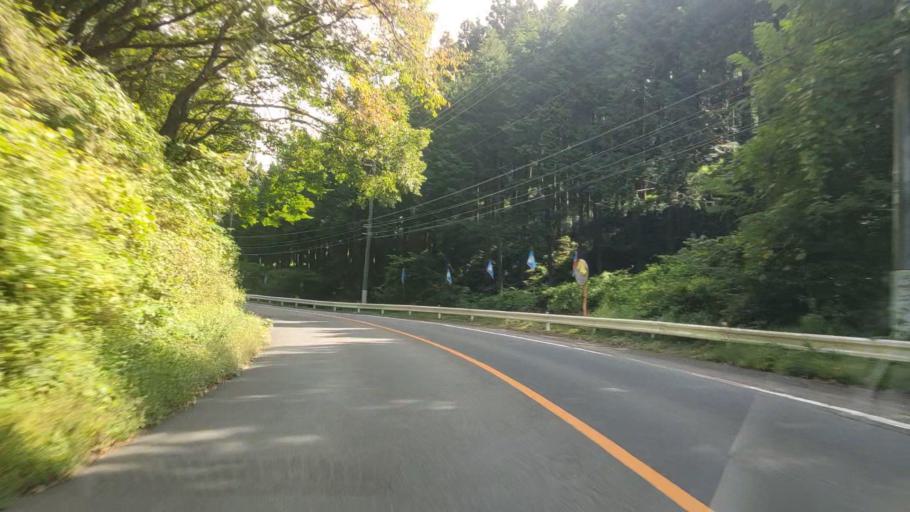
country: JP
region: Gunma
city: Numata
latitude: 36.6300
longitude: 138.9861
